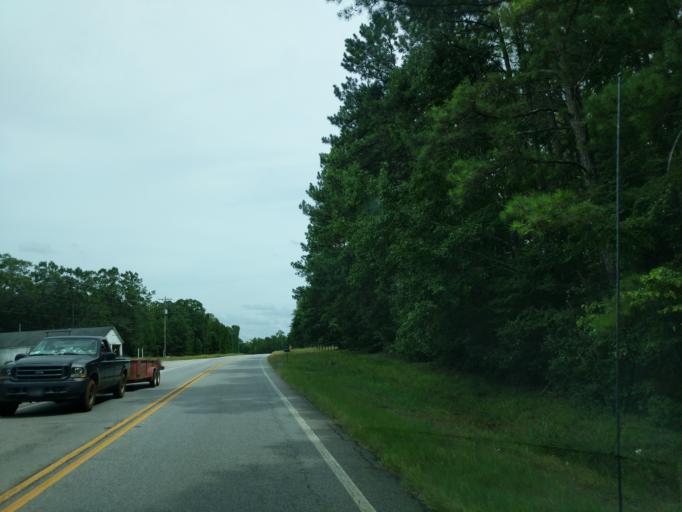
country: US
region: South Carolina
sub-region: Abbeville County
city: Calhoun Falls
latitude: 34.0615
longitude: -82.7192
